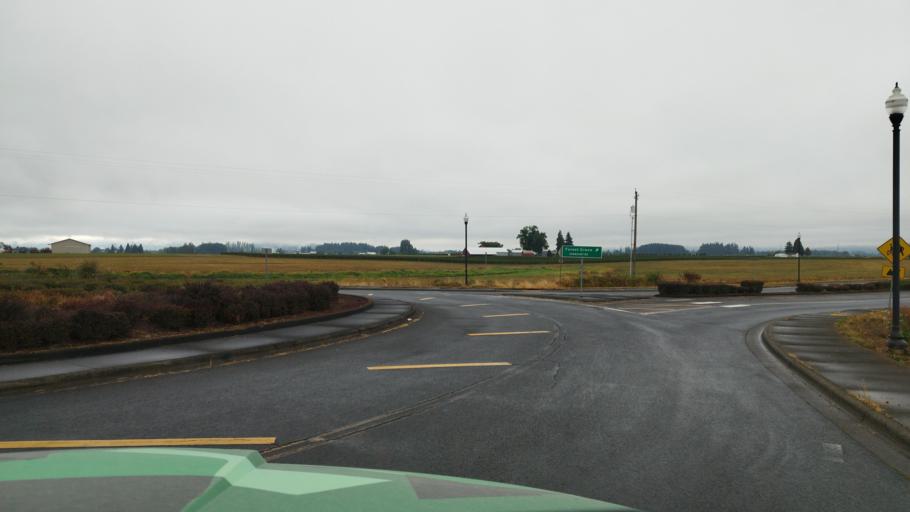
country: US
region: Oregon
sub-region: Washington County
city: Cornelius
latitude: 45.5518
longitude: -123.0642
